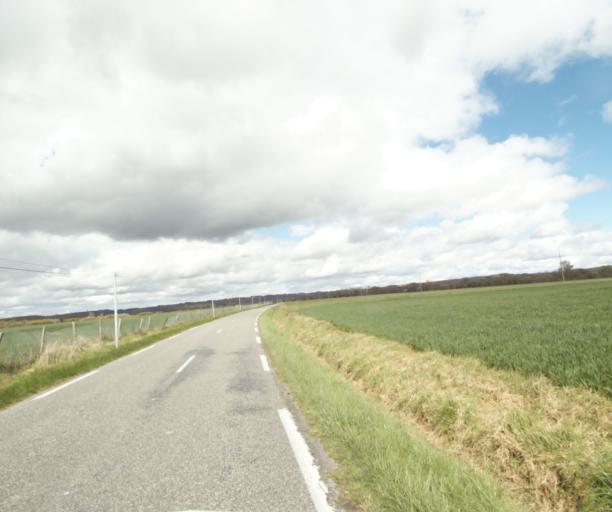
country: FR
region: Midi-Pyrenees
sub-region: Departement de la Haute-Garonne
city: Calmont
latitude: 43.2491
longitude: 1.6365
